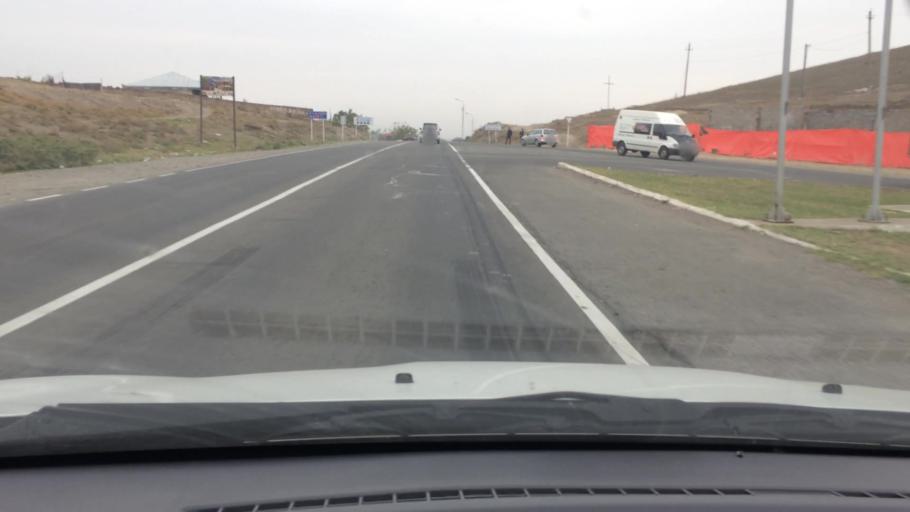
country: GE
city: Naghvarevi
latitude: 41.3634
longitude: 44.8373
